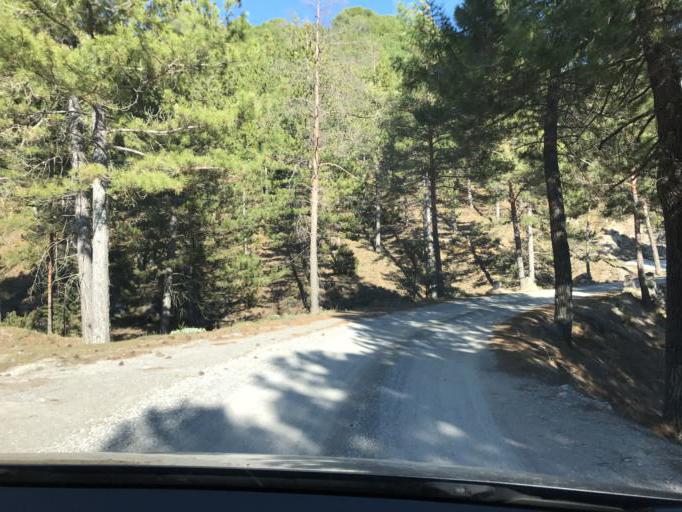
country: ES
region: Andalusia
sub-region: Provincia de Granada
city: Beas de Granada
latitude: 37.2518
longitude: -3.4594
